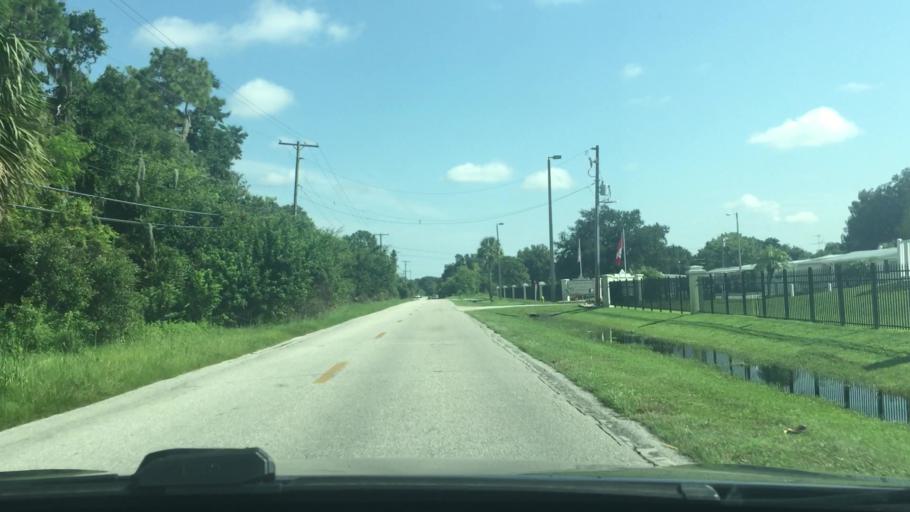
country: US
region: Florida
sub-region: Hillsborough County
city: Ruskin
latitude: 27.6990
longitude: -82.4436
